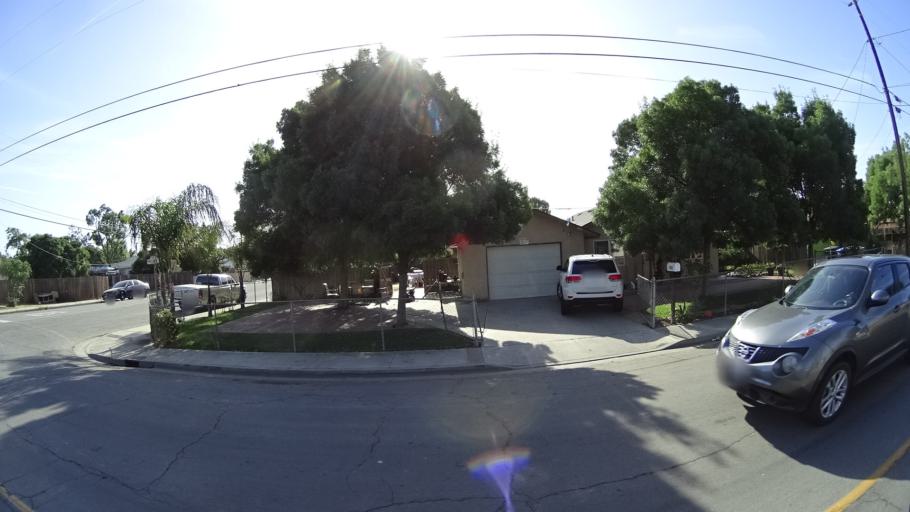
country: US
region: California
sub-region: Kings County
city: Hanford
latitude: 36.3146
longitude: -119.6486
